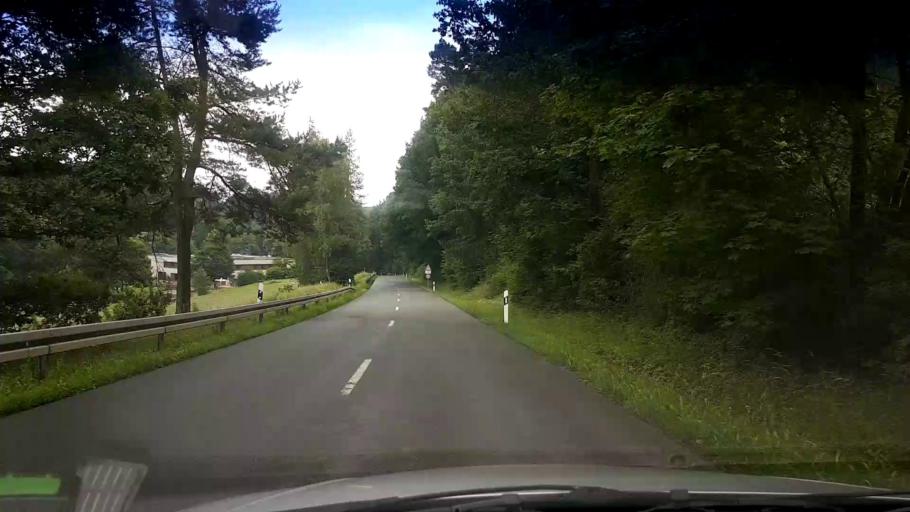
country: DE
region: Bavaria
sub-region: Upper Franconia
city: Kasendorf
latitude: 50.0739
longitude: 11.3277
